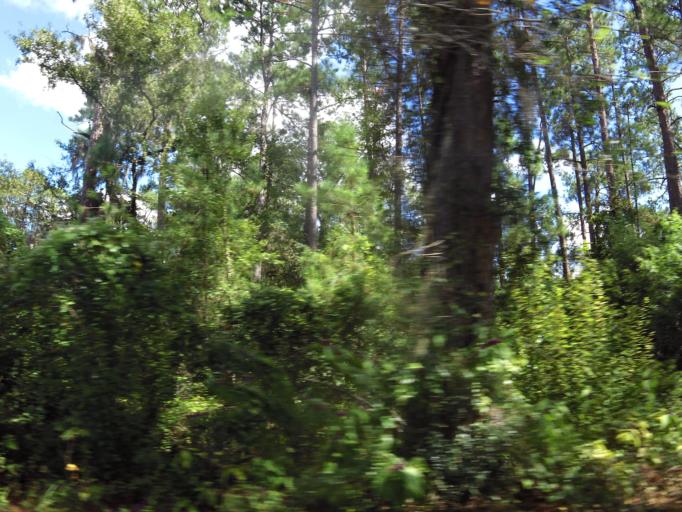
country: US
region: Georgia
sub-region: Clinch County
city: Homerville
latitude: 30.6902
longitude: -82.5617
